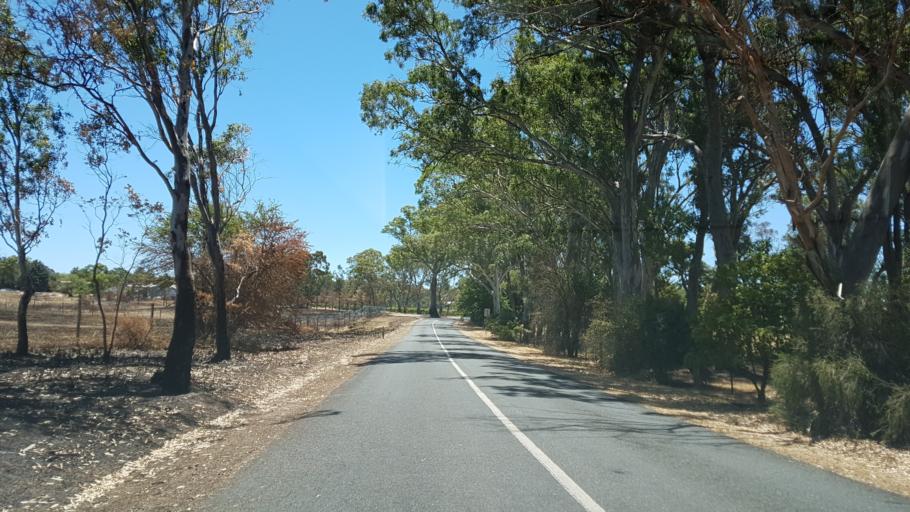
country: AU
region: South Australia
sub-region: Adelaide Hills
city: Lobethal
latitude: -34.8948
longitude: 138.9047
